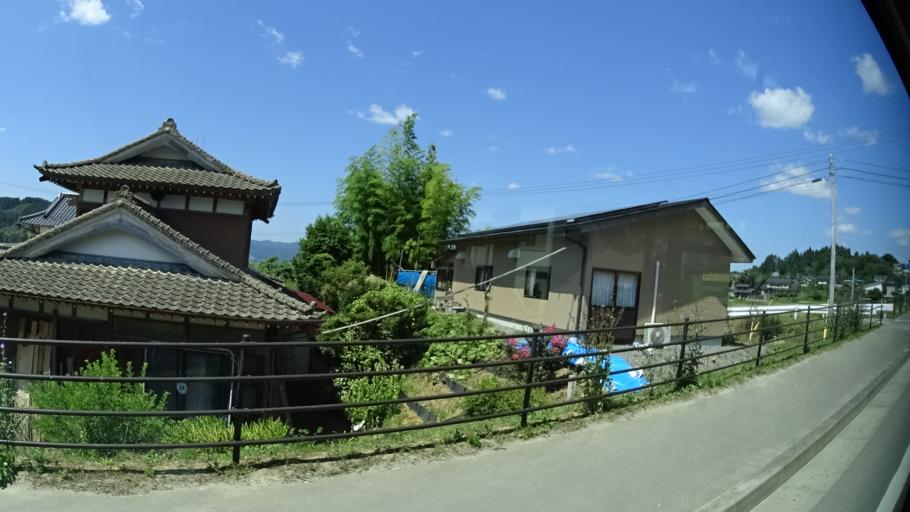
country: JP
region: Iwate
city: Ofunato
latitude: 38.9990
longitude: 141.6905
